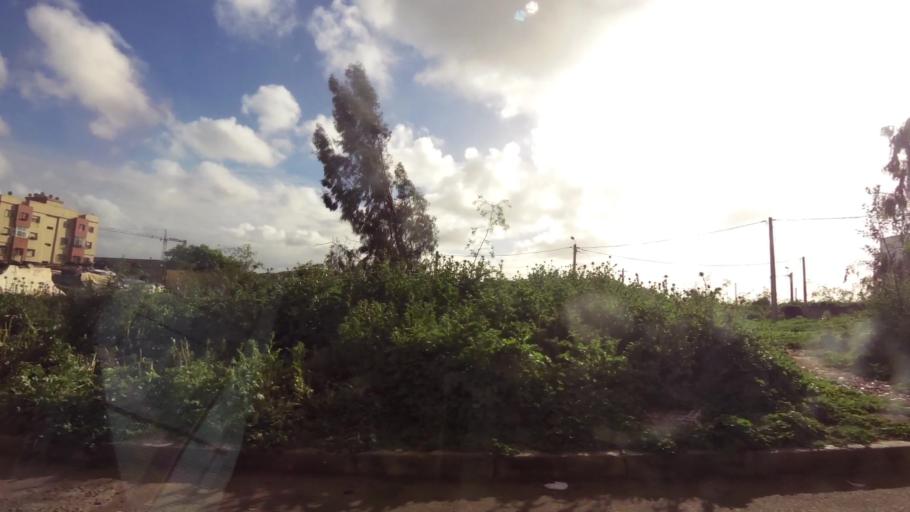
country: MA
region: Grand Casablanca
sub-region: Casablanca
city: Casablanca
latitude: 33.5498
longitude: -7.7050
